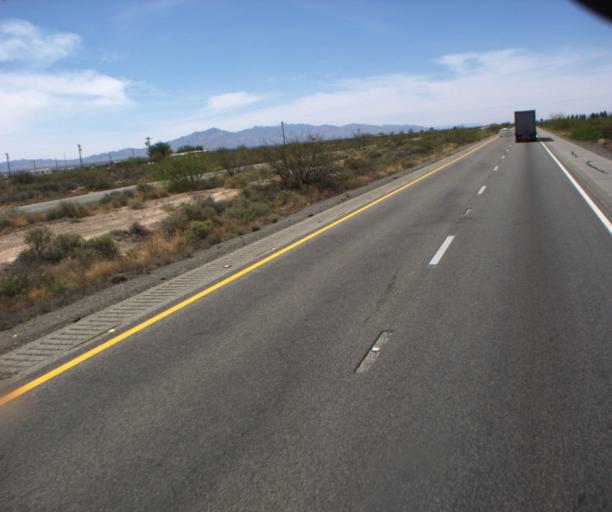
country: US
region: New Mexico
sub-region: Hidalgo County
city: Lordsburg
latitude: 32.2611
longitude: -109.2174
